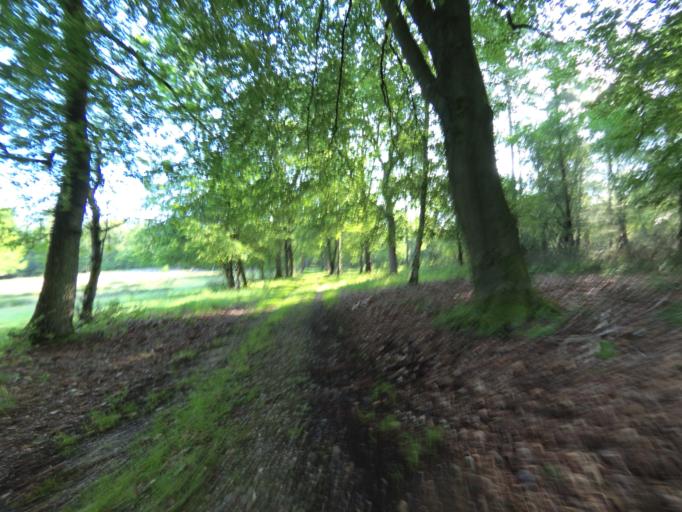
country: NL
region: Gelderland
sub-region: Gemeente Apeldoorn
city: Beekbergen
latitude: 52.1344
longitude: 5.8727
